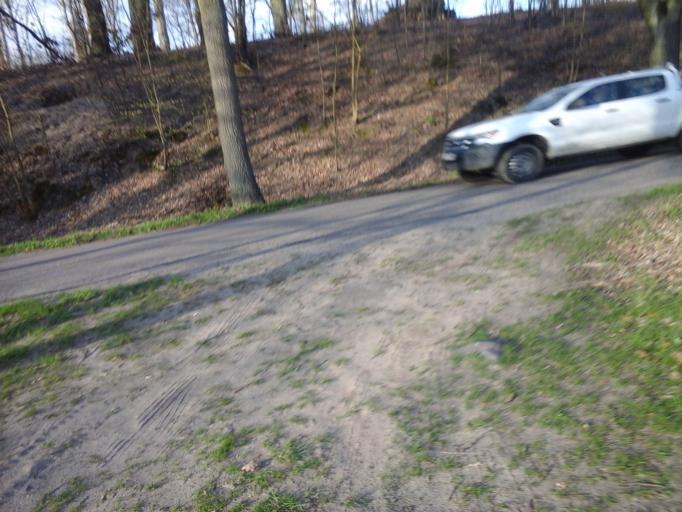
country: PL
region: West Pomeranian Voivodeship
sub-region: Powiat choszczenski
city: Bierzwnik
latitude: 53.0093
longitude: 15.6249
